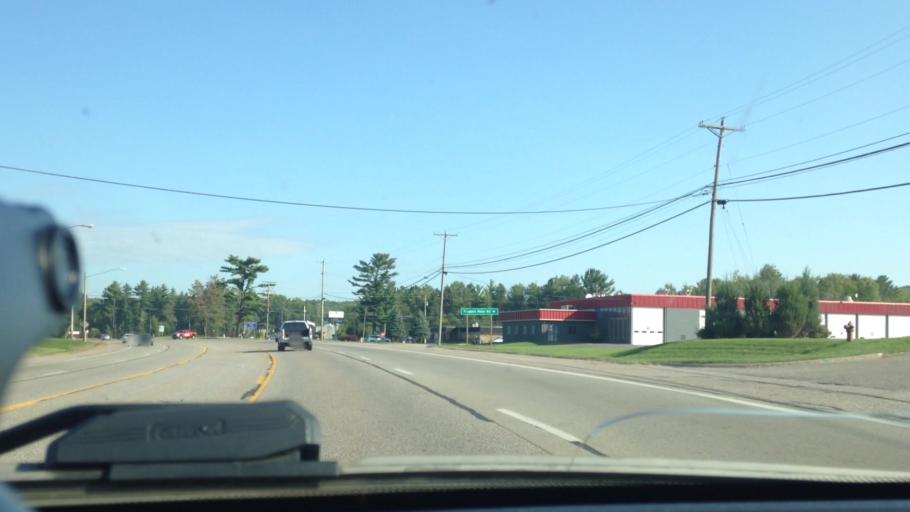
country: US
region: Michigan
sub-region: Dickinson County
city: Iron Mountain
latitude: 45.8432
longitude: -88.0490
